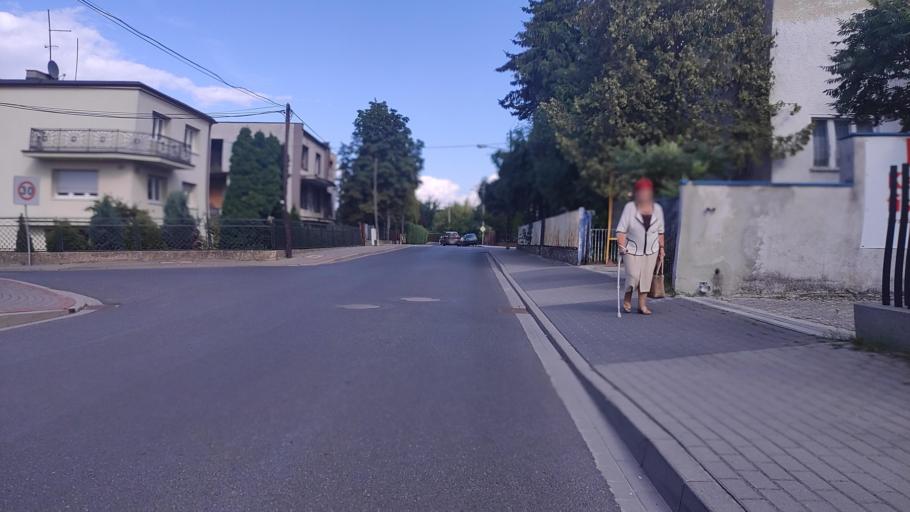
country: PL
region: Greater Poland Voivodeship
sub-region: Powiat poznanski
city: Swarzedz
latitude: 52.4127
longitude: 17.0884
